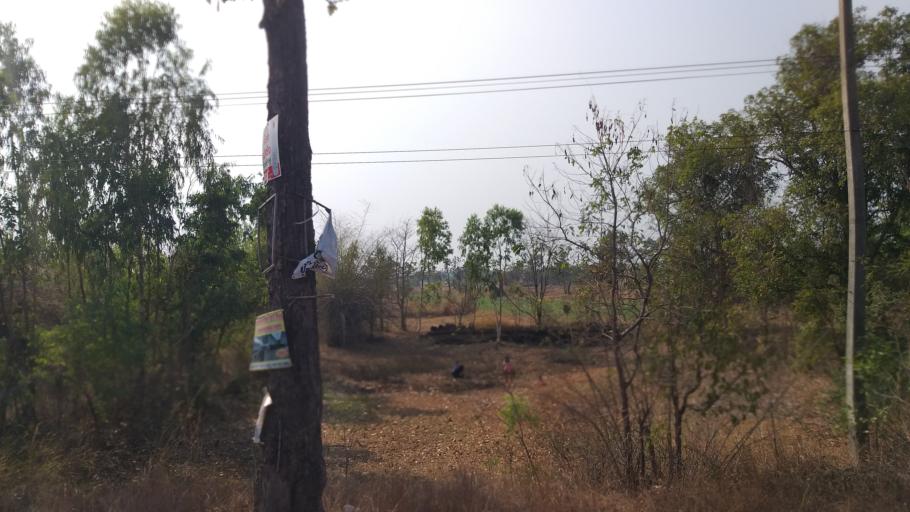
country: TH
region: Changwat Udon Thani
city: Ban Dung
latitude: 17.5876
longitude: 103.2463
